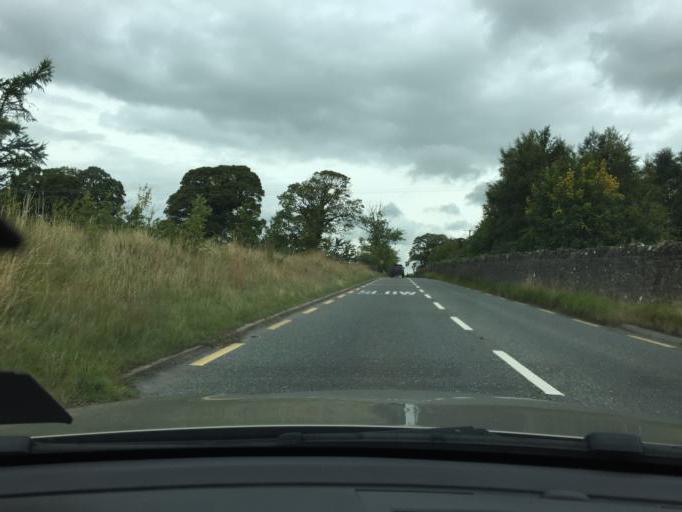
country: IE
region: Leinster
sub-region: Kildare
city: Maynooth
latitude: 53.3902
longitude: -6.5765
